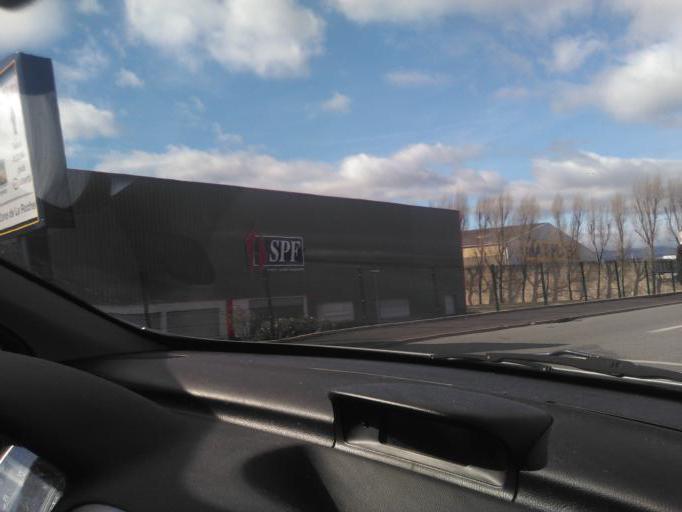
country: FR
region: Auvergne
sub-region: Departement du Puy-de-Dome
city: Le Cendre
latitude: 45.7386
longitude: 3.1729
